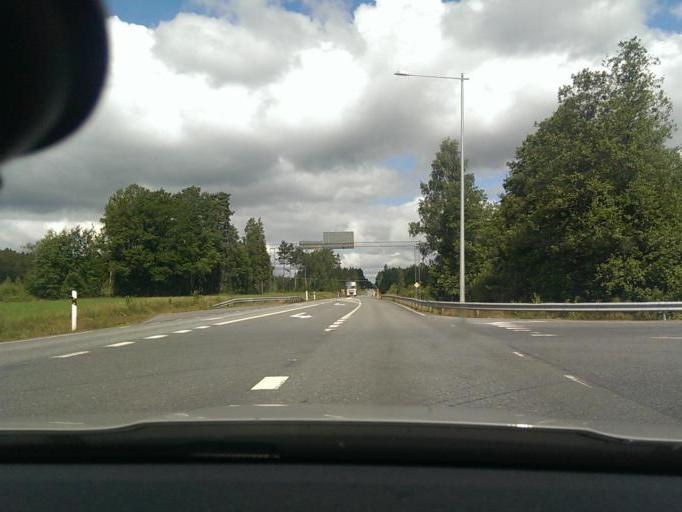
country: SE
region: Joenkoeping
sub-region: Varnamo Kommun
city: Varnamo
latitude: 57.2091
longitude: 14.0263
